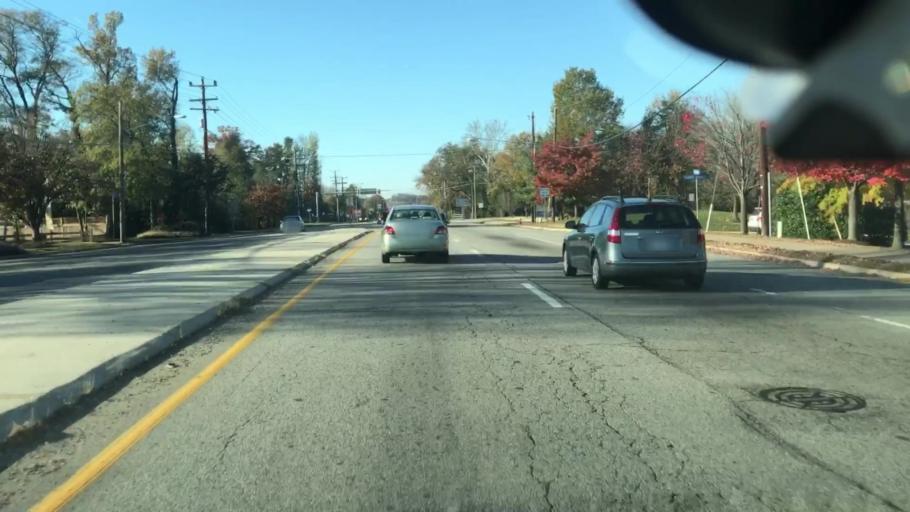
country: US
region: Virginia
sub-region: Fairfax County
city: Mount Vernon
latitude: 38.7257
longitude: -77.1149
